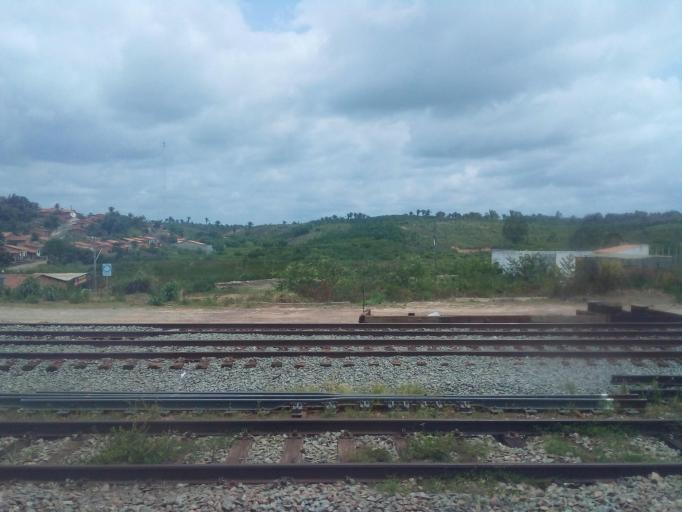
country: BR
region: Maranhao
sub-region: Santa Ines
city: Santa Ines
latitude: -3.6694
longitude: -45.8433
